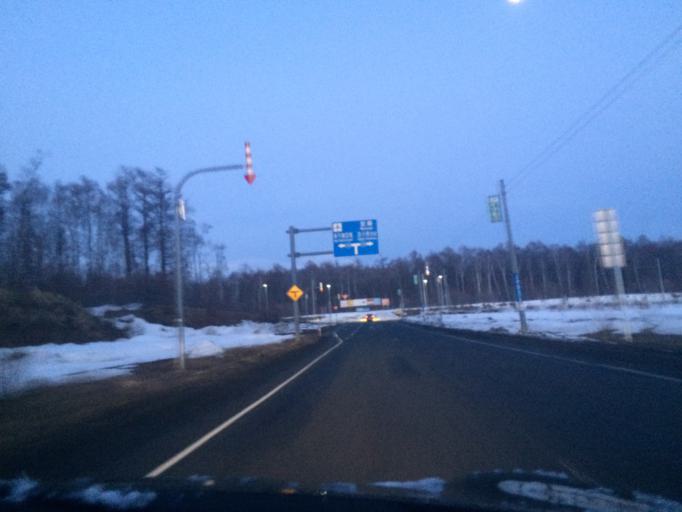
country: JP
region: Hokkaido
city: Chitose
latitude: 42.7637
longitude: 141.6786
